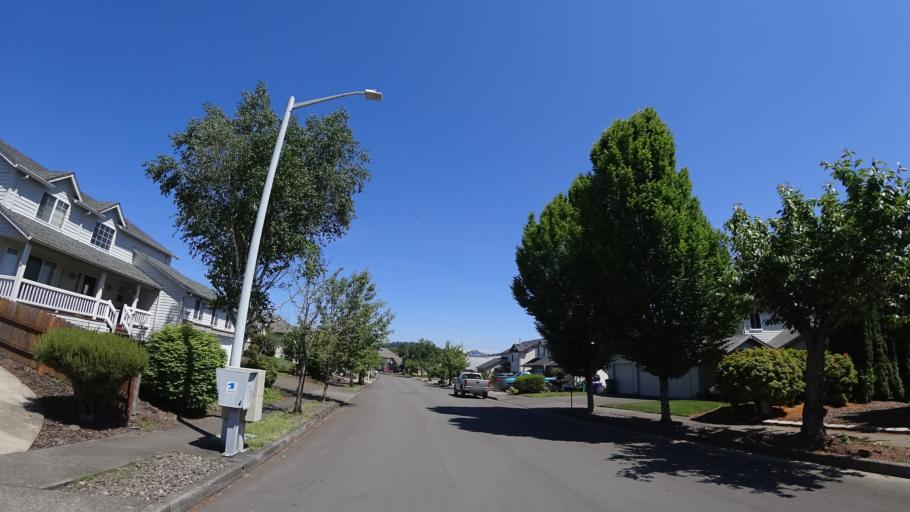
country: US
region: Oregon
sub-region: Multnomah County
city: Gresham
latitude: 45.4765
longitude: -122.4747
